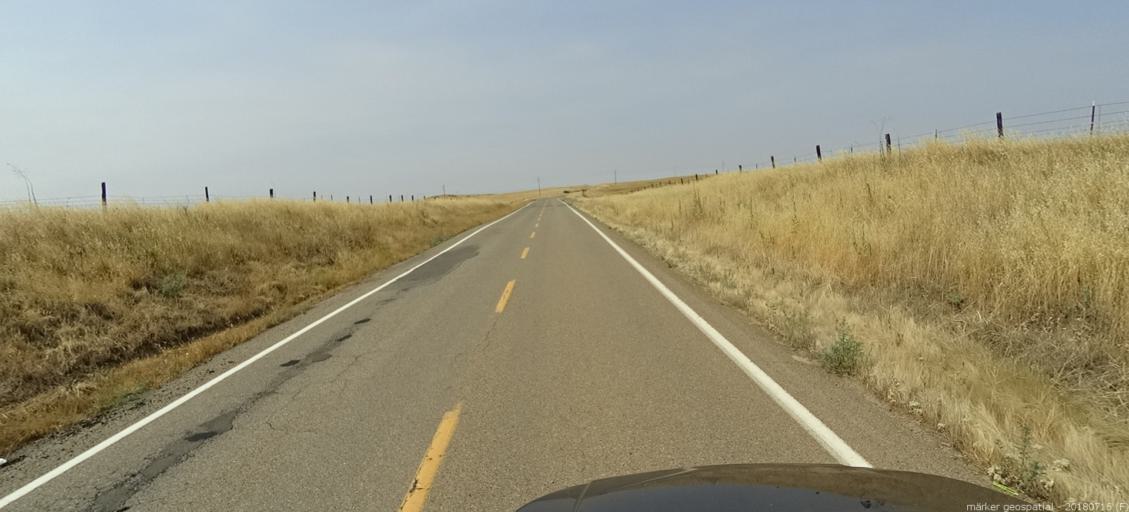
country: US
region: California
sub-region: Madera County
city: Bonadelle Ranchos-Madera Ranchos
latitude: 37.1008
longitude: -119.9428
